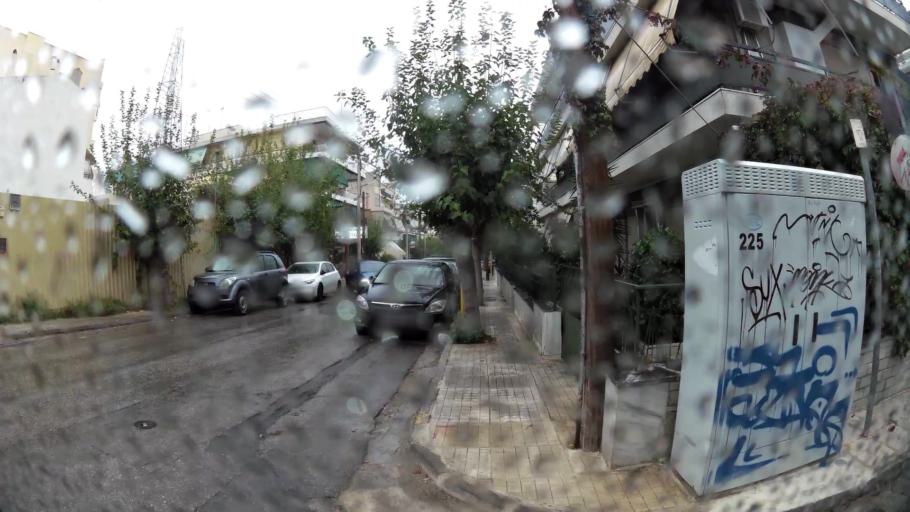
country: GR
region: Attica
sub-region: Nomarchia Athinas
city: Chaidari
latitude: 38.0058
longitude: 23.6626
